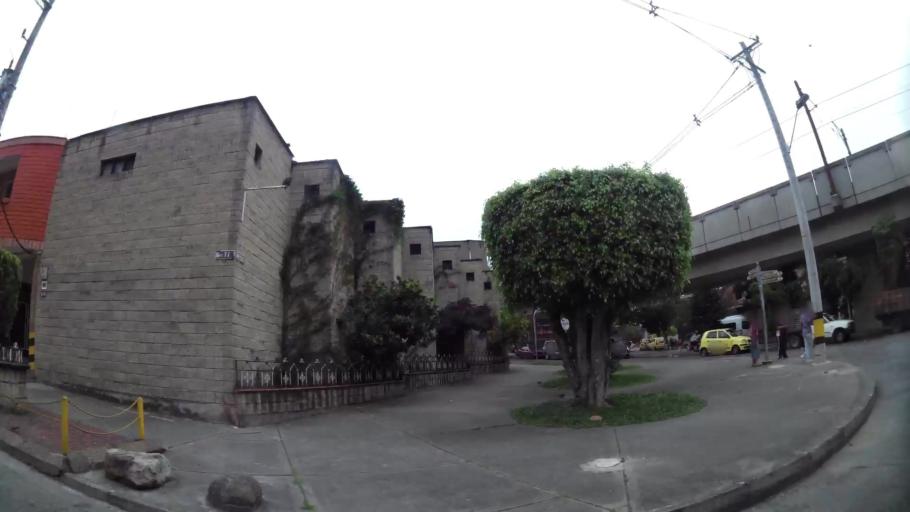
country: CO
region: Antioquia
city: Medellin
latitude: 6.2674
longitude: -75.5626
